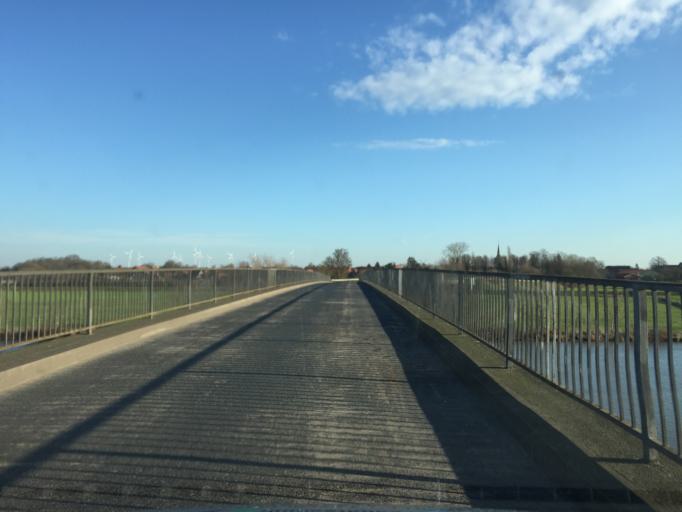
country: DE
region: Lower Saxony
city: Landesbergen
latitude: 52.5595
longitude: 9.1114
